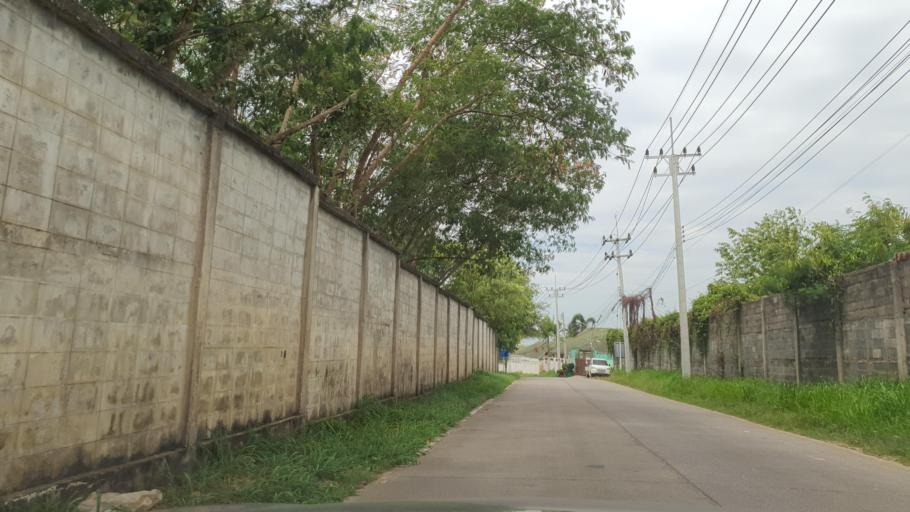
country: TH
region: Chon Buri
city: Bang Lamung
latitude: 12.9835
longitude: 100.9440
